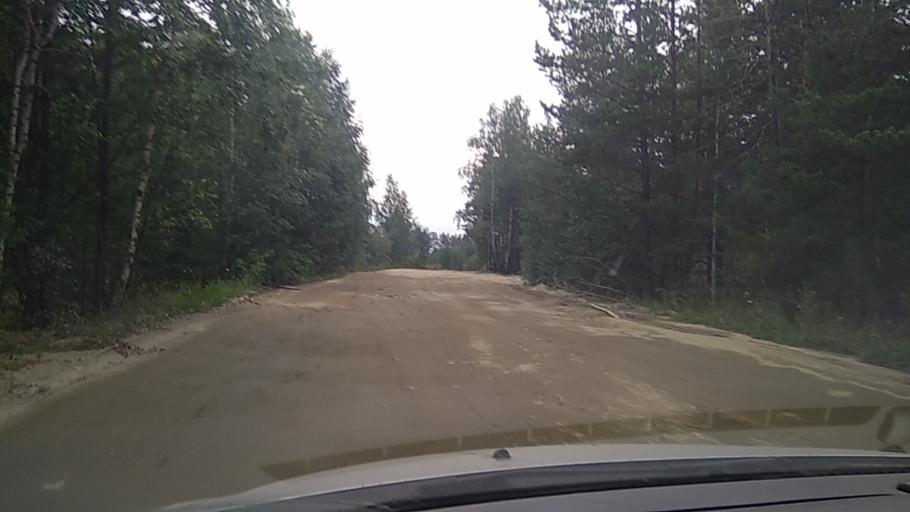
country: RU
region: Chelyabinsk
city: Kyshtym
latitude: 55.6808
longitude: 60.5733
